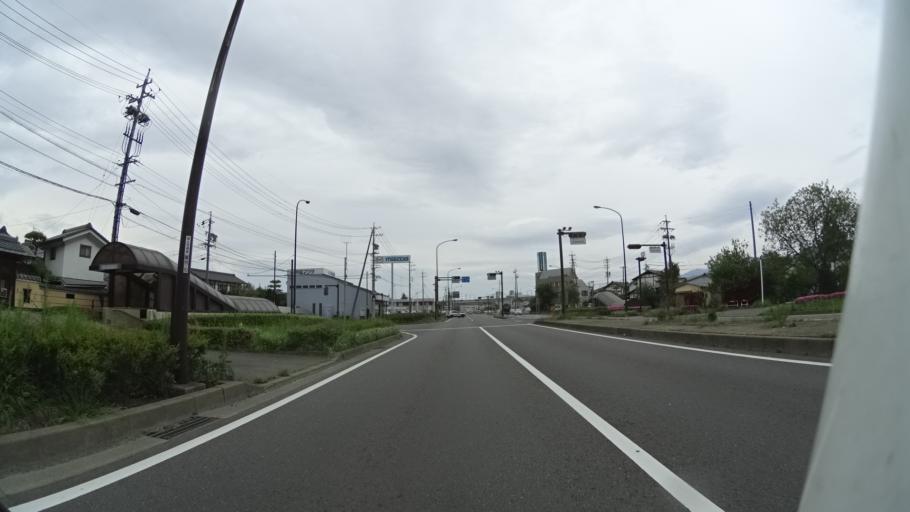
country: JP
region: Nagano
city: Nagano-shi
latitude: 36.5439
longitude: 138.1255
